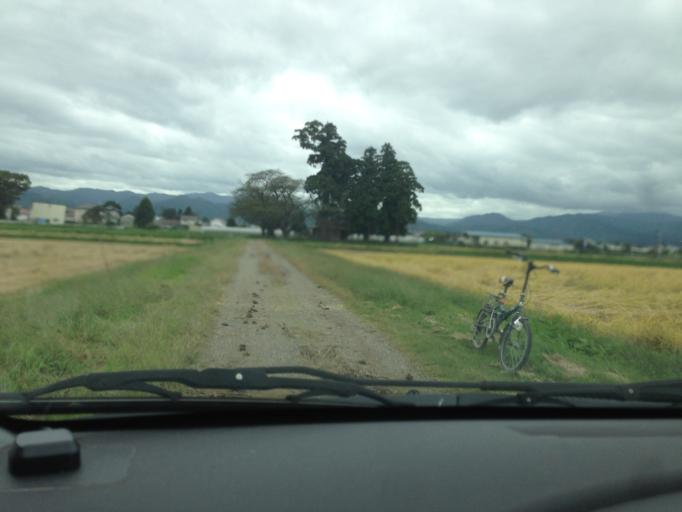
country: JP
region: Fukushima
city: Kitakata
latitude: 37.4757
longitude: 139.8532
